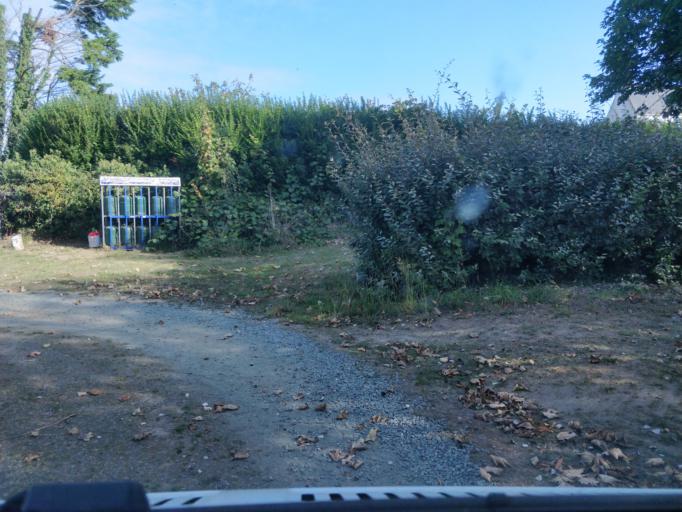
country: FR
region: Brittany
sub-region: Departement du Finistere
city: Plouhinec
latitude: 48.0068
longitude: -4.4936
